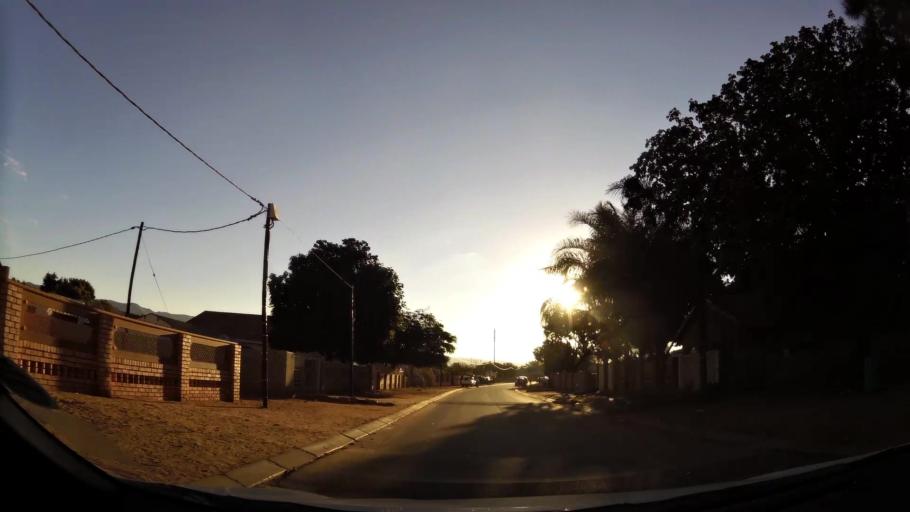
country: ZA
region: Limpopo
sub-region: Waterberg District Municipality
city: Mokopane
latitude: -24.1487
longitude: 28.9846
